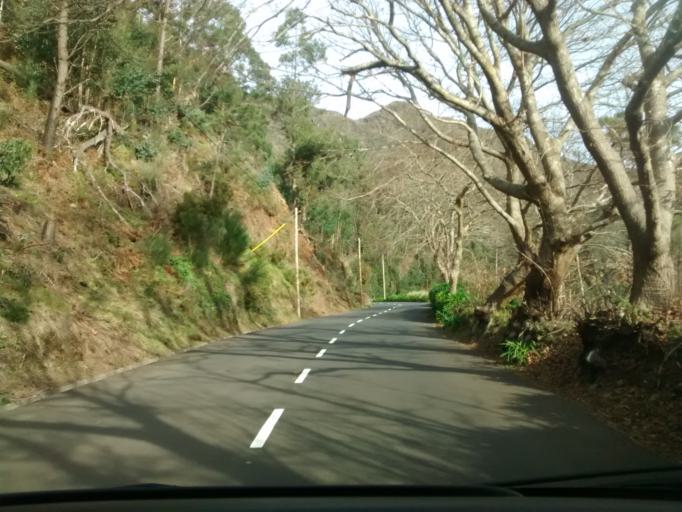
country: PT
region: Madeira
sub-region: Sao Vicente
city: Sao Vicente
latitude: 32.7444
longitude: -17.0246
